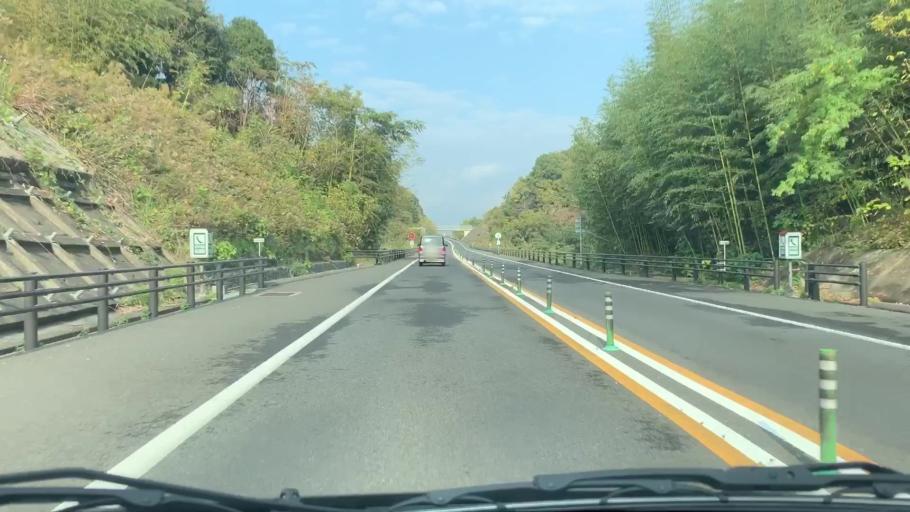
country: JP
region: Nagasaki
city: Sasebo
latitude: 33.0216
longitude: 129.7338
